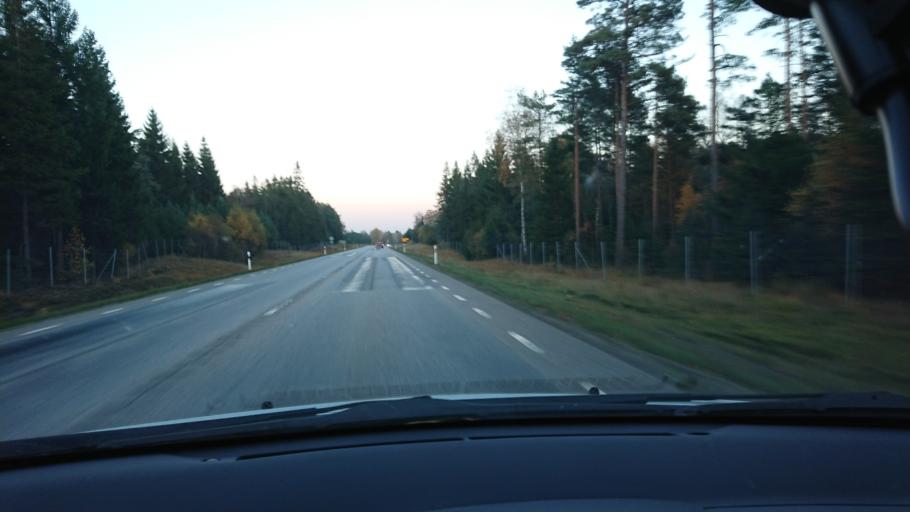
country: SE
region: Halland
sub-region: Laholms Kommun
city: Knared
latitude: 56.7367
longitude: 13.4360
